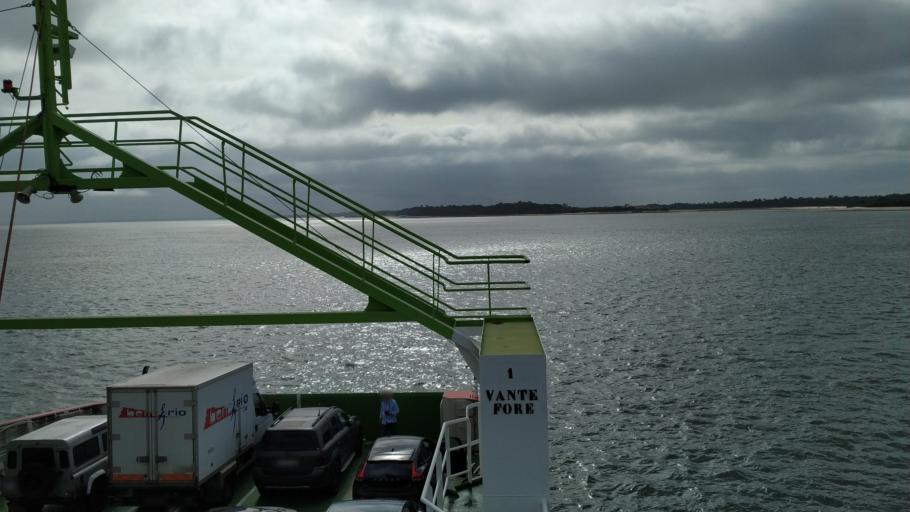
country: PT
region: Setubal
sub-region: Setubal
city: Setubal
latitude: 38.4992
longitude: -8.8885
